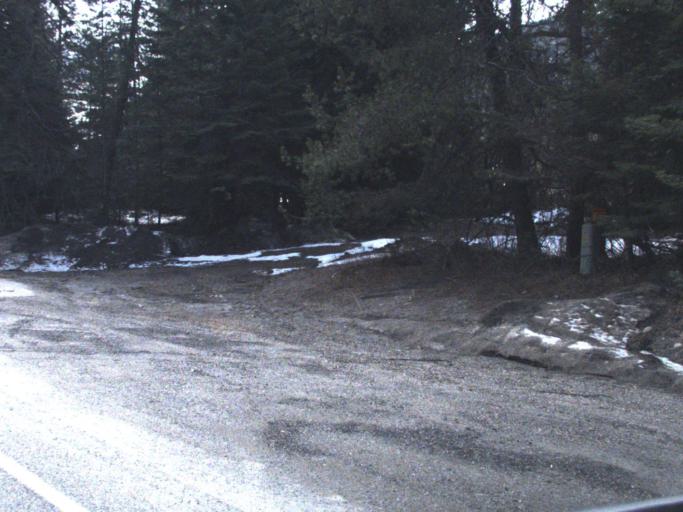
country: US
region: Washington
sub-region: Stevens County
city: Chewelah
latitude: 48.6110
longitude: -117.3650
